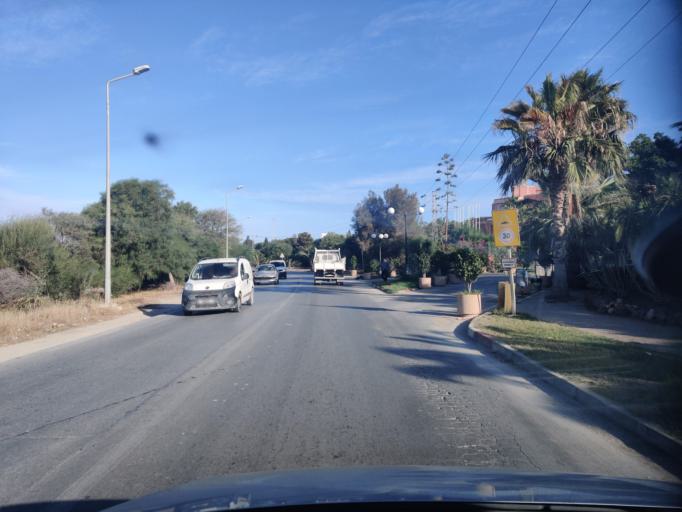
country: TN
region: Tunis
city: Al Marsa
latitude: 36.9383
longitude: 10.2525
